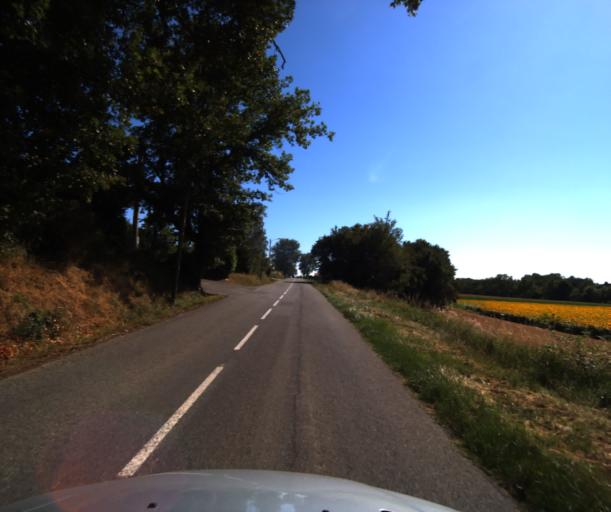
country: FR
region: Midi-Pyrenees
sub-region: Departement de la Haute-Garonne
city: Eaunes
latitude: 43.4268
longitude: 1.3210
